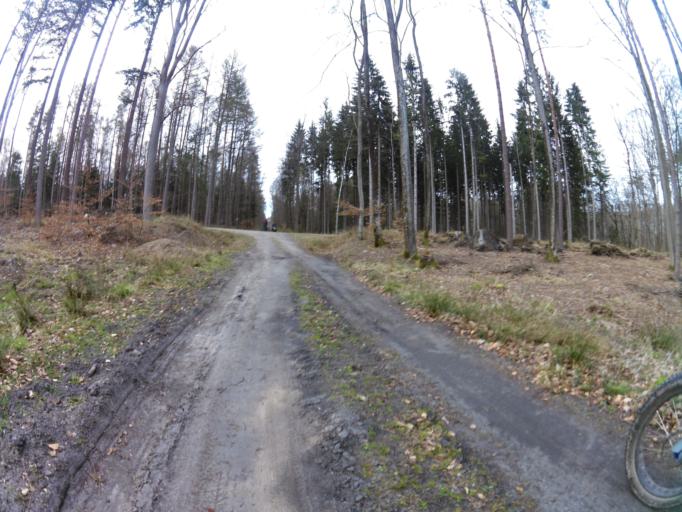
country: PL
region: West Pomeranian Voivodeship
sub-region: Powiat szczecinecki
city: Bialy Bor
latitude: 53.8929
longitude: 16.7178
